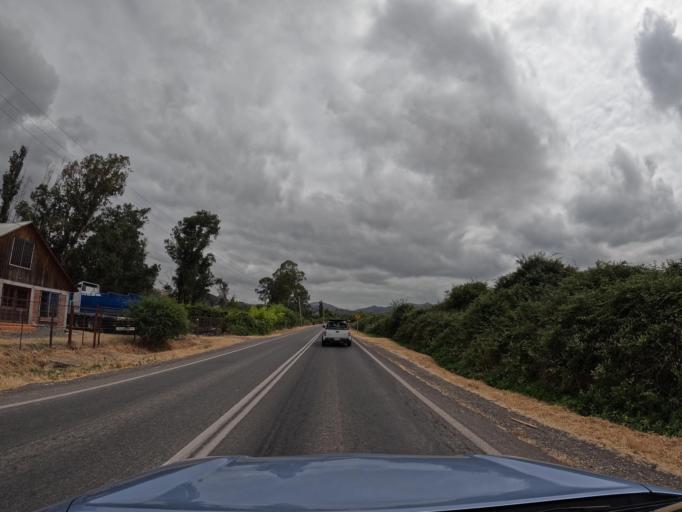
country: CL
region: Maule
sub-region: Provincia de Curico
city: Teno
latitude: -34.8517
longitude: -71.1927
